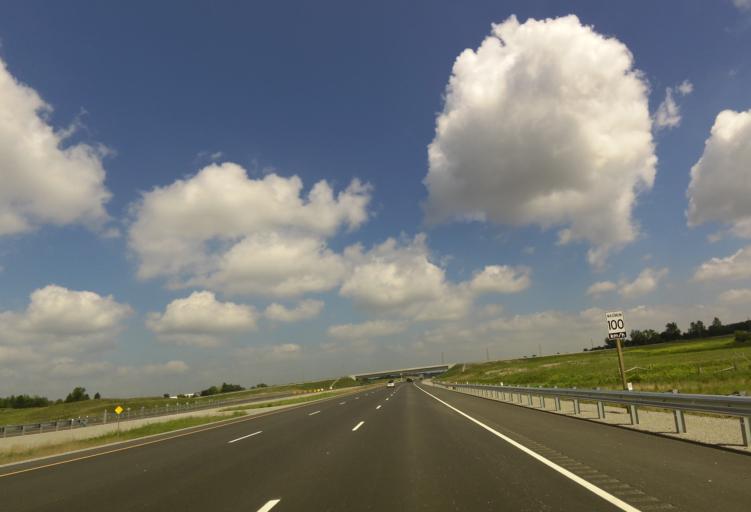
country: CA
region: Ontario
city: Pickering
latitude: 43.9353
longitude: -79.0754
